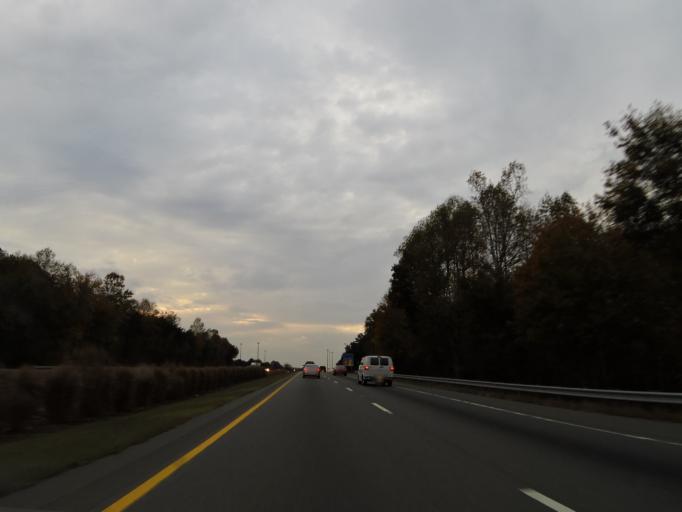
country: US
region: North Carolina
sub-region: Burke County
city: Hildebran
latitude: 35.7056
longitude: -81.4157
